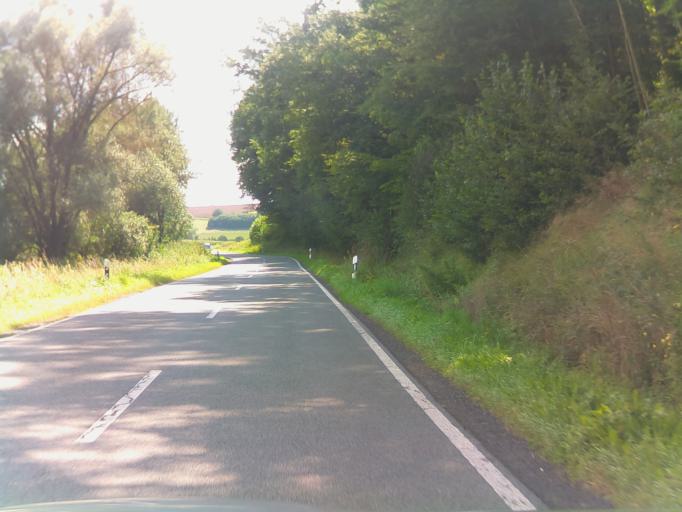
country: DE
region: Bavaria
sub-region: Regierungsbezirk Unterfranken
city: Untermerzbach
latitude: 50.0971
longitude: 10.8551
